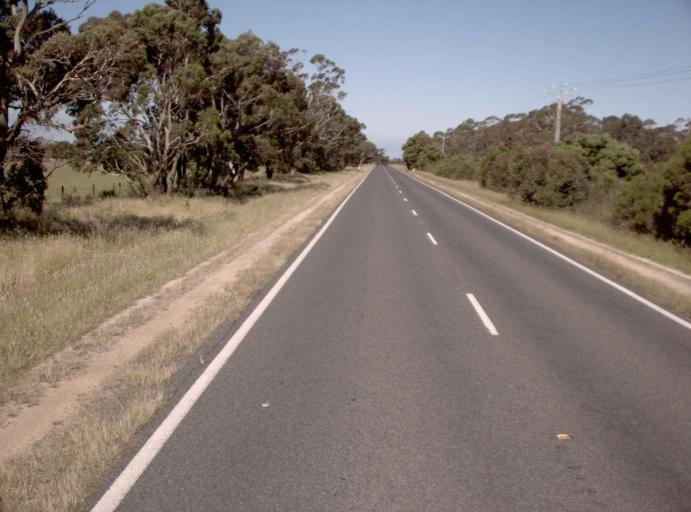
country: AU
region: Victoria
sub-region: Latrobe
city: Morwell
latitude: -38.6327
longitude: 146.5515
